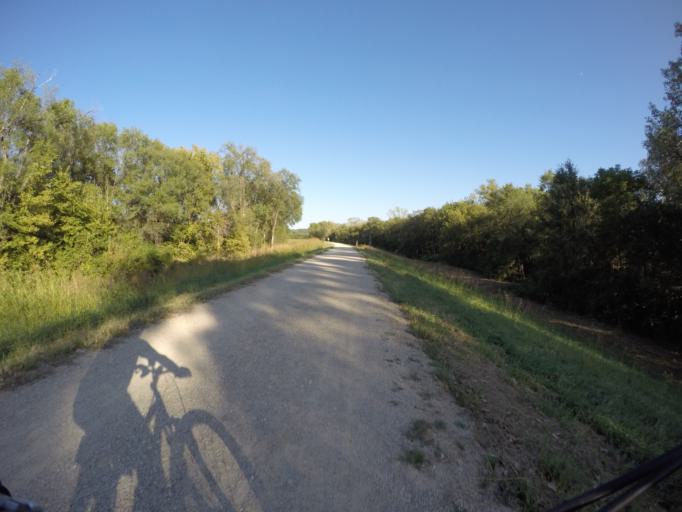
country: US
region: Kansas
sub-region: Riley County
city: Manhattan
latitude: 39.1713
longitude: -96.5725
